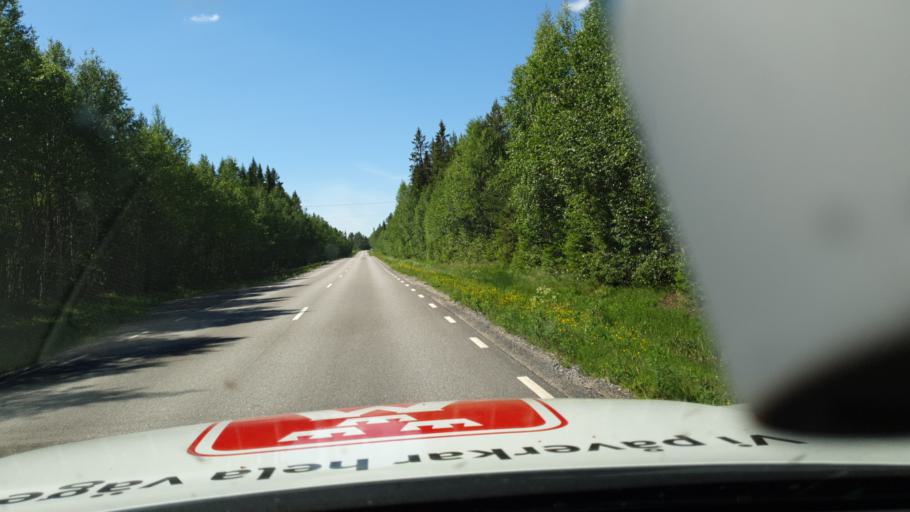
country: SE
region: Jaemtland
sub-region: Harjedalens Kommun
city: Sveg
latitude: 62.0971
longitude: 13.6440
